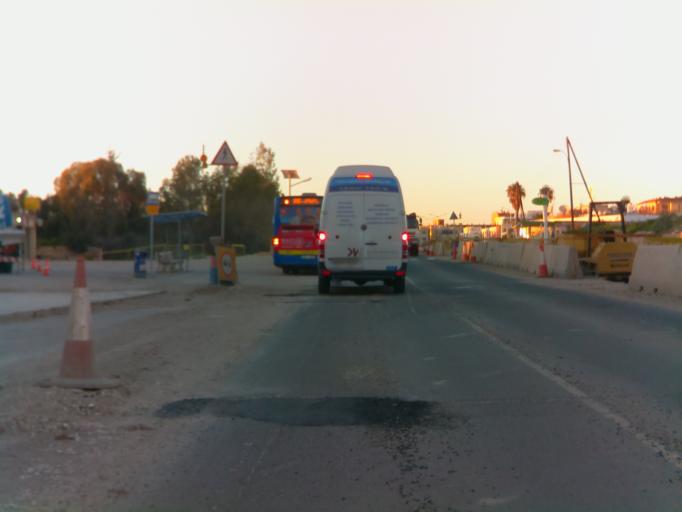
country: CY
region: Pafos
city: Paphos
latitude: 34.7726
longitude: 32.4096
